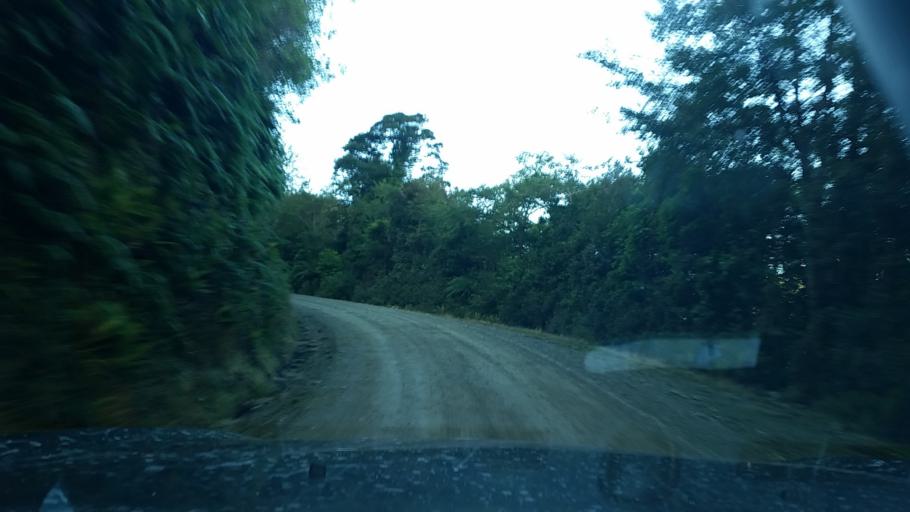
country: NZ
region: Marlborough
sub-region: Marlborough District
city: Picton
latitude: -41.0980
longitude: 174.1346
